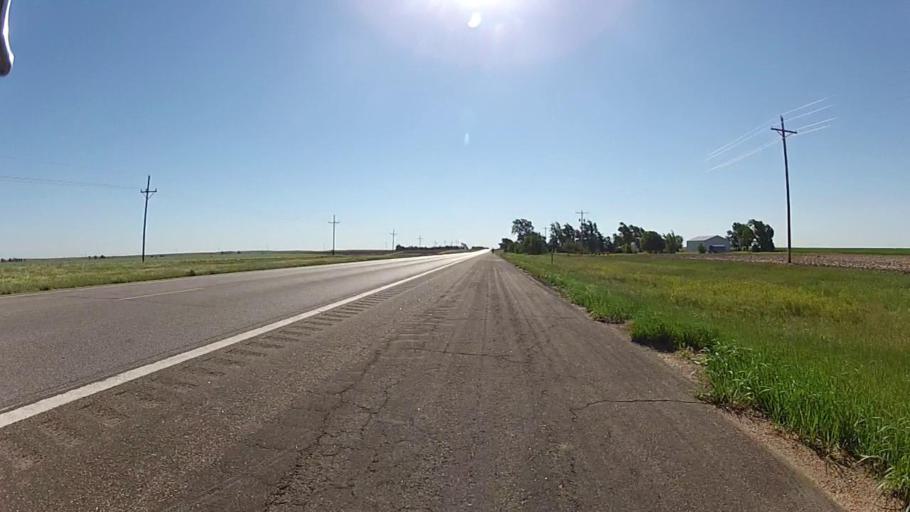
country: US
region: Kansas
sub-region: Kiowa County
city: Greensburg
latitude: 37.5864
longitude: -99.6000
